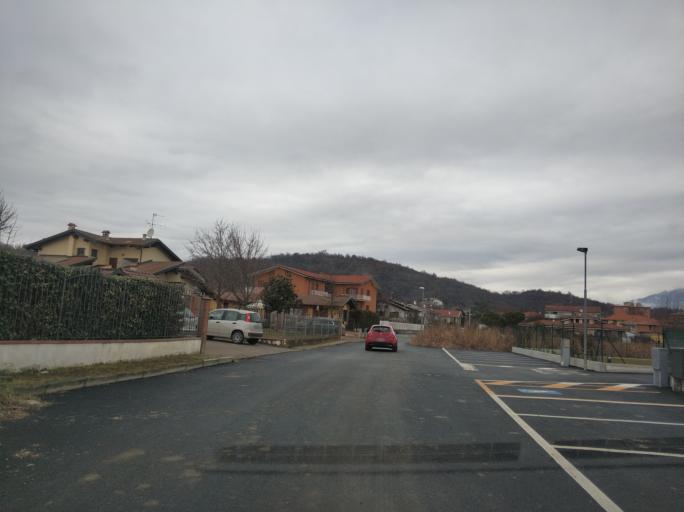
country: IT
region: Piedmont
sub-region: Provincia di Torino
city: Pavone Canavese
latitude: 45.4363
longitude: 7.8670
